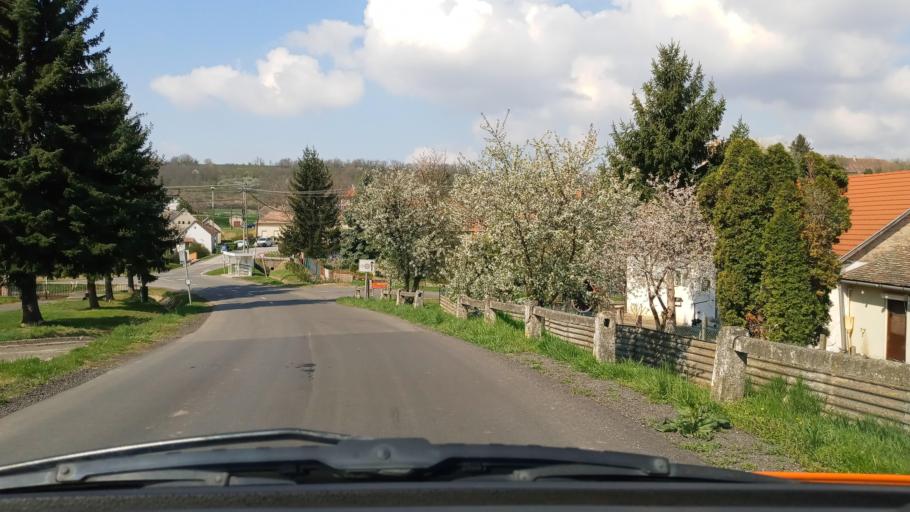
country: HU
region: Baranya
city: Pecsvarad
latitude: 46.1009
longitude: 18.4604
